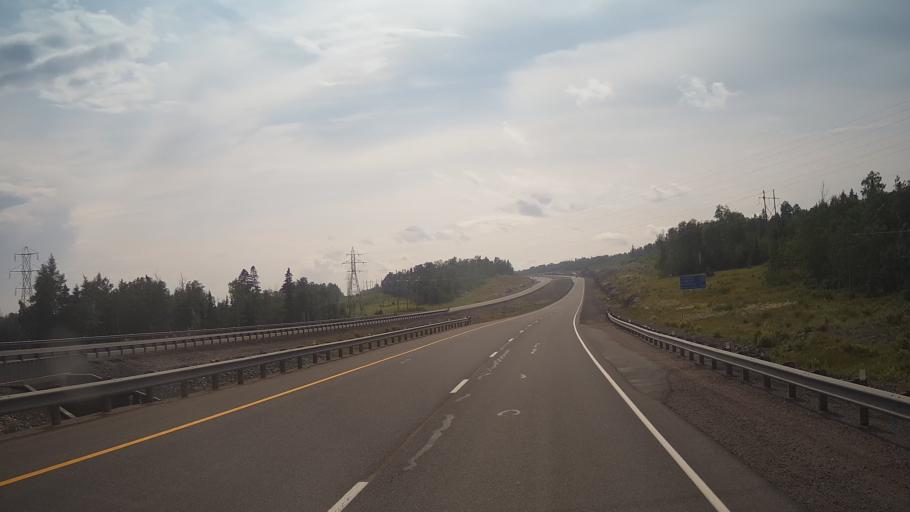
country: CA
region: Ontario
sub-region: Thunder Bay District
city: Thunder Bay
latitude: 48.5686
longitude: -88.8396
